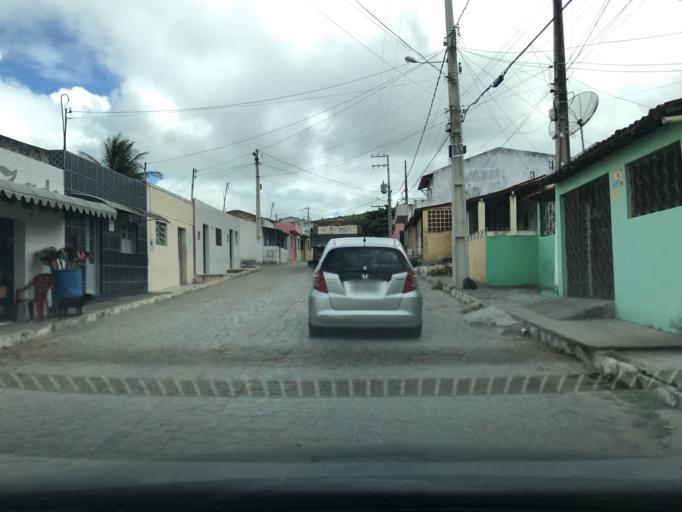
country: BR
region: Pernambuco
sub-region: Bezerros
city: Bezerros
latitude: -8.2301
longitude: -35.7595
